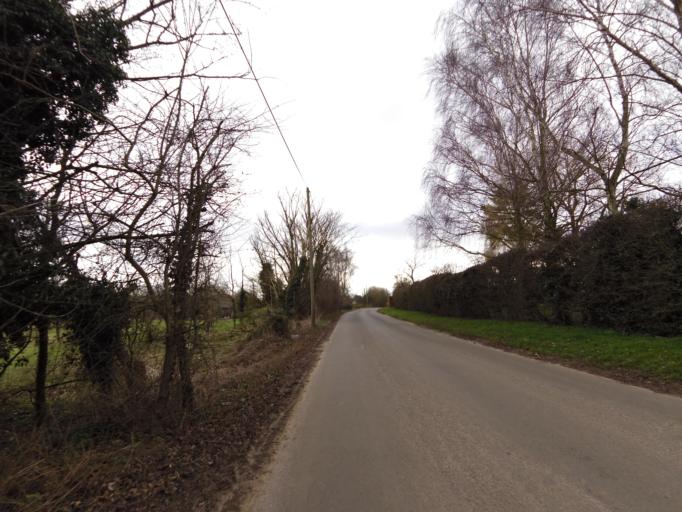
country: GB
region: England
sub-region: Suffolk
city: Woodbridge
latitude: 52.0371
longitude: 1.3142
